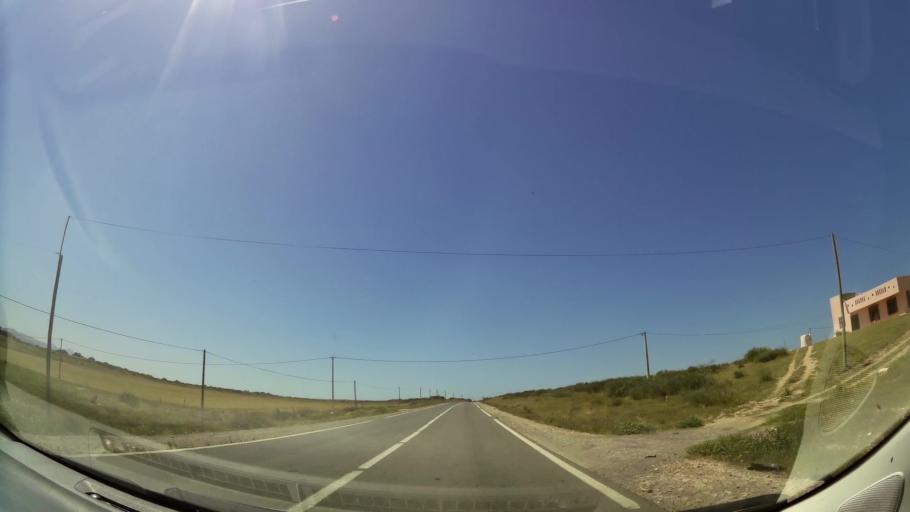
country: MA
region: Oriental
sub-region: Berkane-Taourirt
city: Madagh
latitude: 35.1266
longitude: -2.3899
